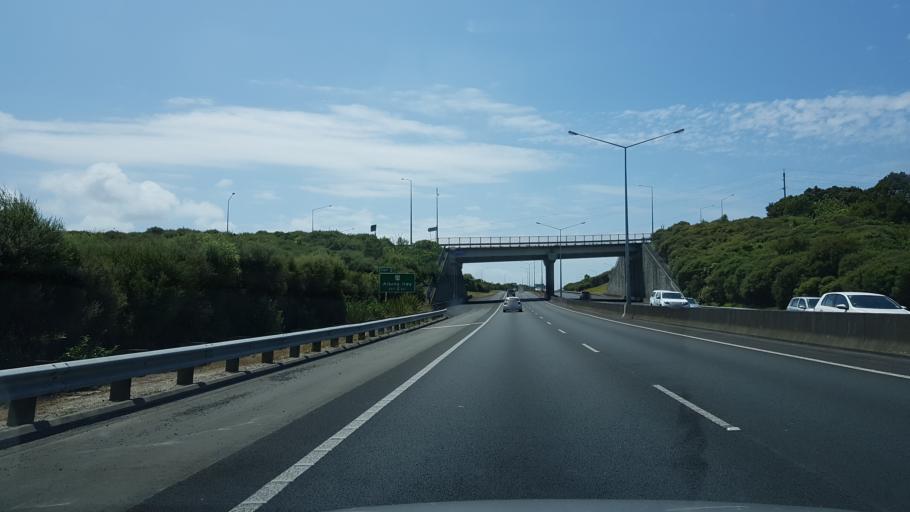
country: NZ
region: Auckland
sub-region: Auckland
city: North Shore
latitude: -36.7731
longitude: 174.6850
